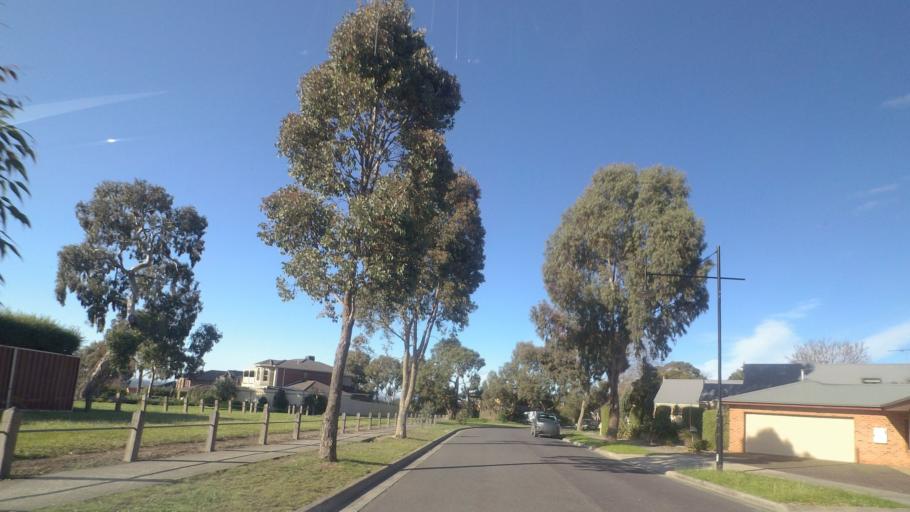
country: AU
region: Victoria
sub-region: Banyule
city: Watsonia North
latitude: -37.6939
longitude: 145.0748
